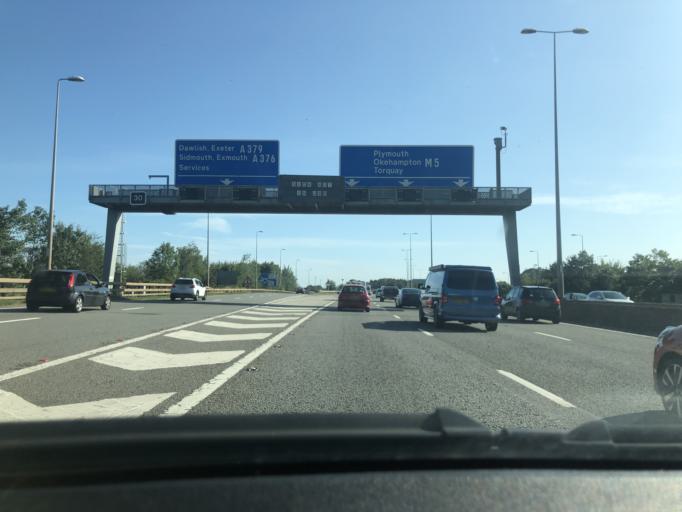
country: GB
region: England
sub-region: Devon
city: Topsham
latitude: 50.7168
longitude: -3.4621
